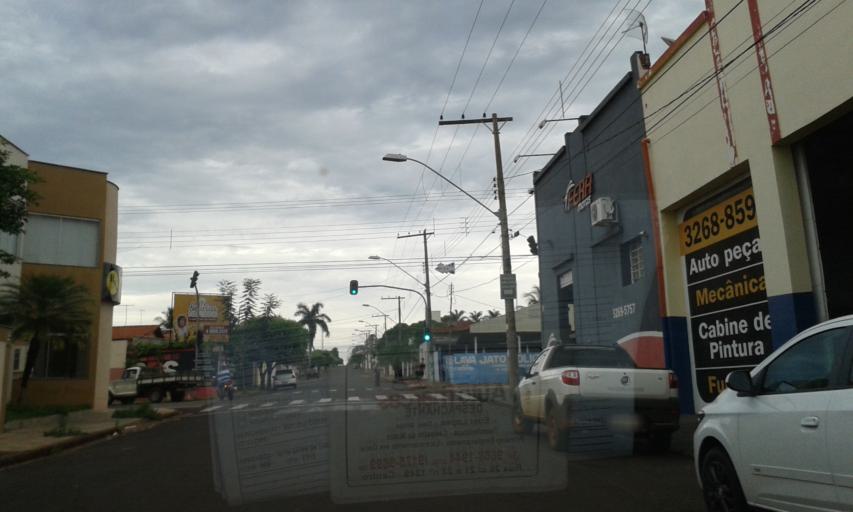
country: BR
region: Minas Gerais
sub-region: Ituiutaba
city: Ituiutaba
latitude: -18.9819
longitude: -49.4593
